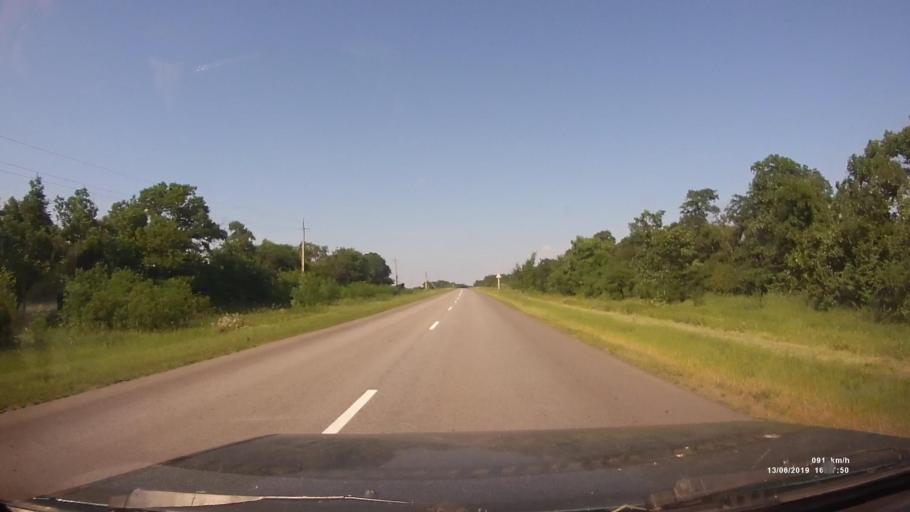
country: RU
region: Rostov
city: Kazanskaya
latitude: 49.8167
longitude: 41.1898
